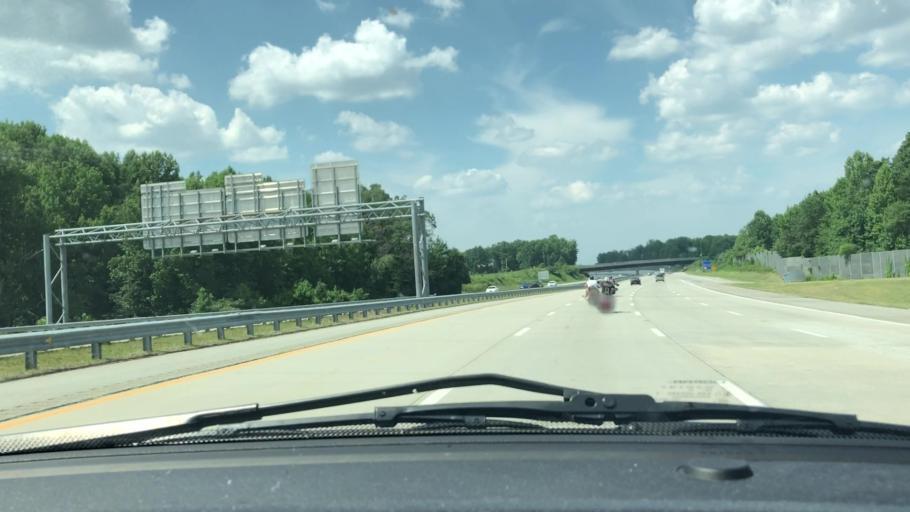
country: US
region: North Carolina
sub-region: Guilford County
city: Jamestown
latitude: 36.0097
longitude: -79.8529
